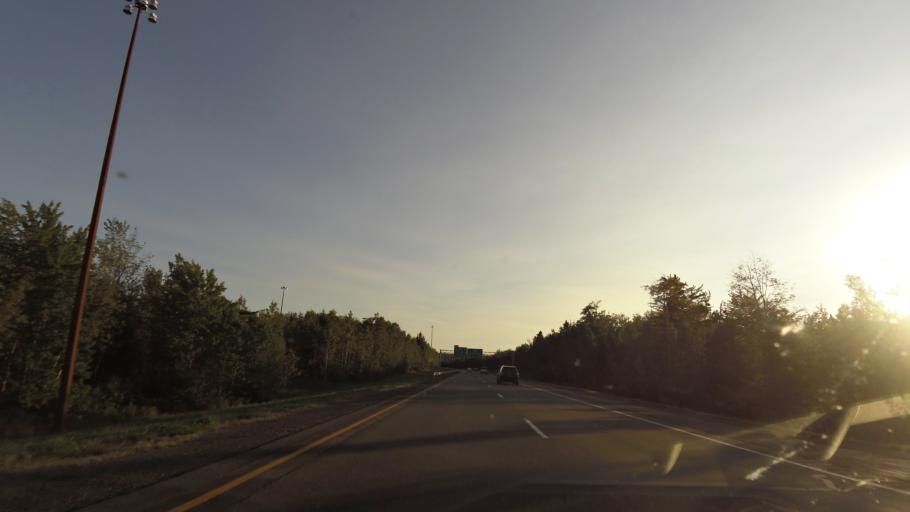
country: CA
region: New Brunswick
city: Salisbury
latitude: 46.0015
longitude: -65.1330
